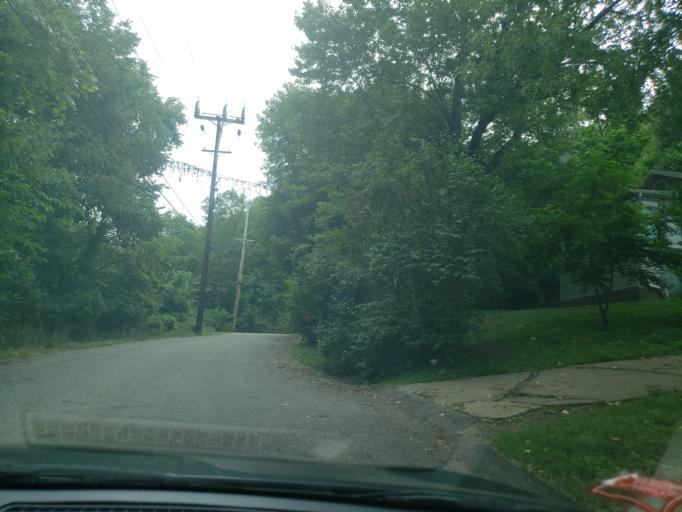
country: US
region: Pennsylvania
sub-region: Allegheny County
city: Ben Avon
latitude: 40.5184
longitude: -80.0861
